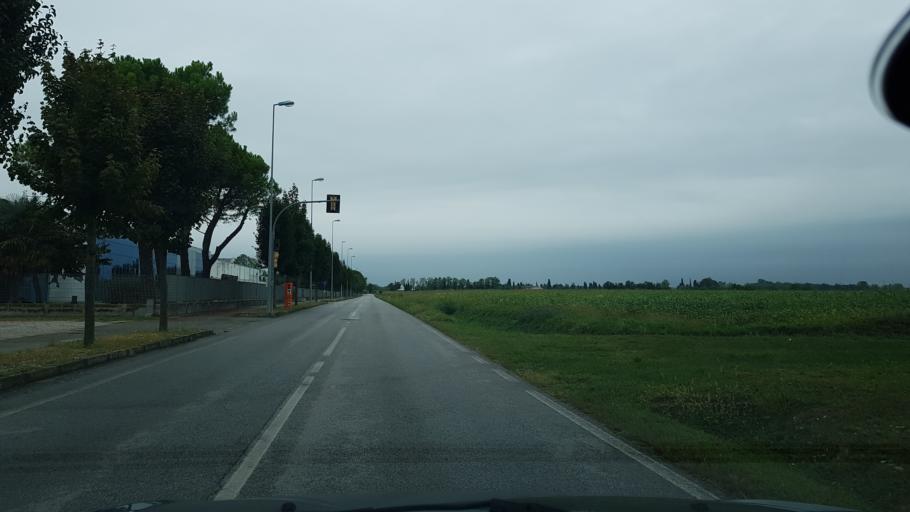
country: IT
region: Friuli Venezia Giulia
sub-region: Provincia di Udine
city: Trivignano Udinese
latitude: 45.9530
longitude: 13.3392
